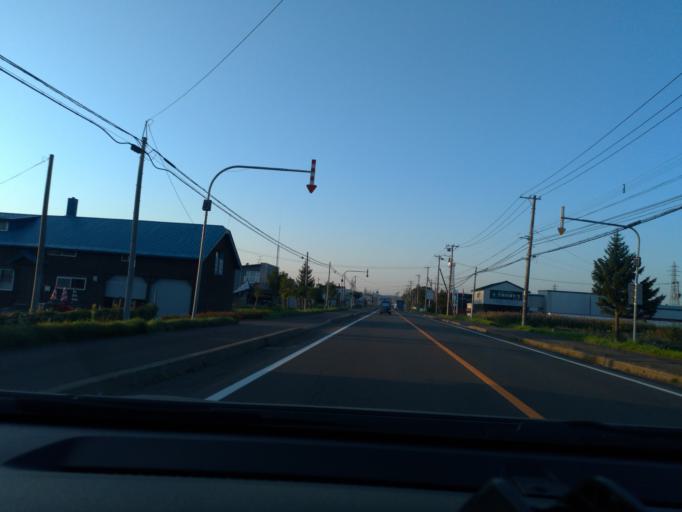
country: JP
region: Hokkaido
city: Tobetsu
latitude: 43.2060
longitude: 141.5200
